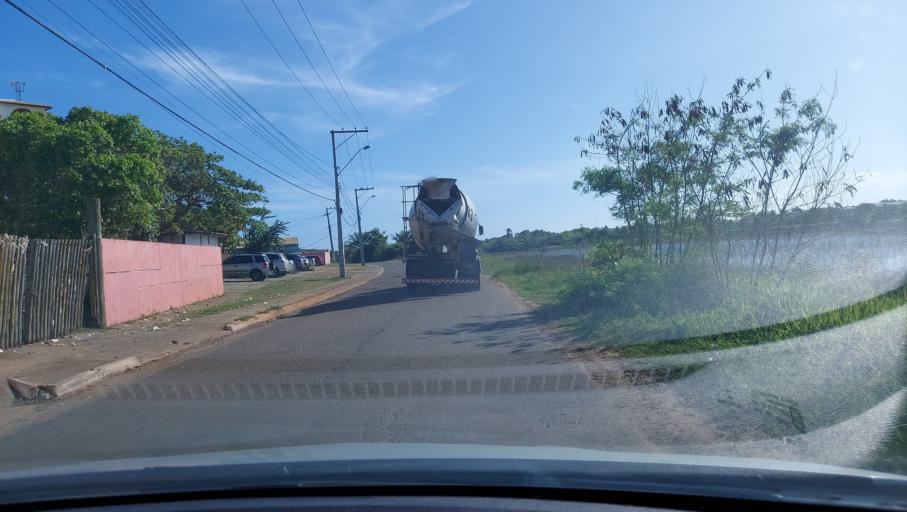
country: BR
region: Bahia
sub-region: Mata De Sao Joao
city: Mata de Sao Joao
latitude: -12.6209
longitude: -38.0473
